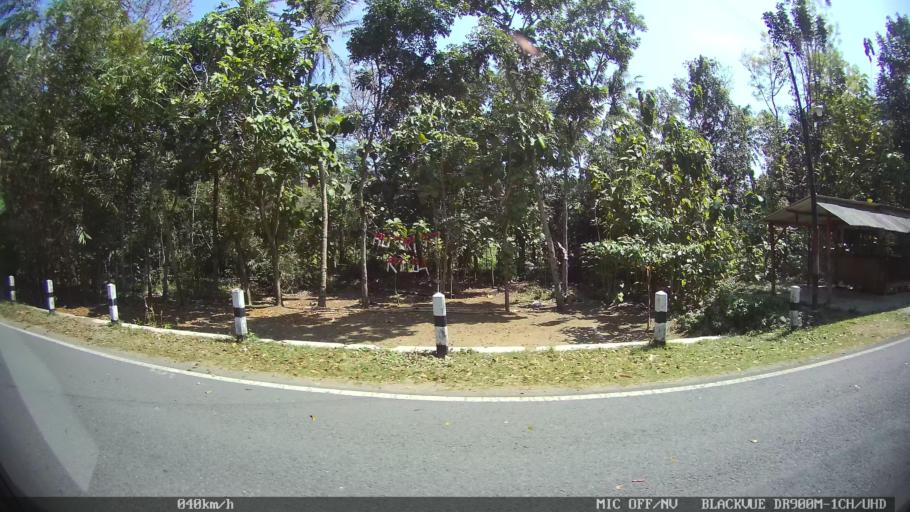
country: ID
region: Daerah Istimewa Yogyakarta
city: Pundong
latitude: -7.9572
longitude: 110.3795
